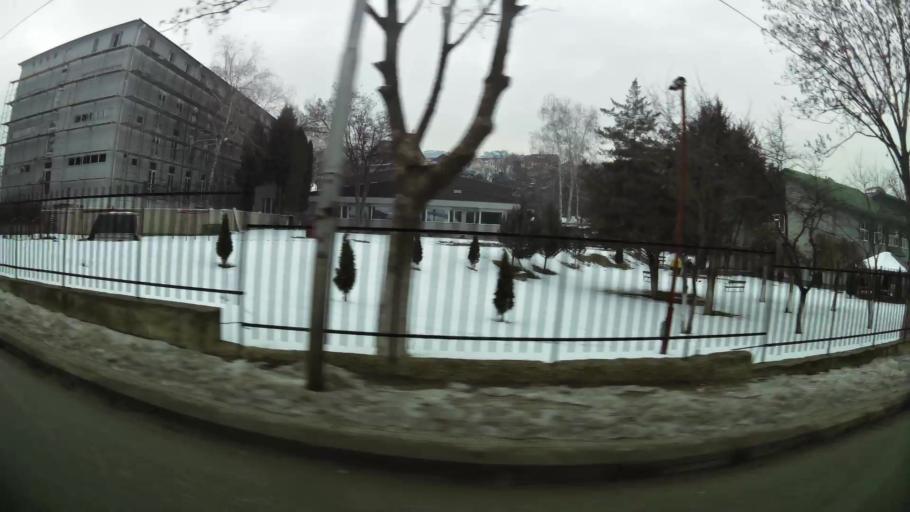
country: MK
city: Kondovo
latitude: 42.0118
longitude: 21.3066
